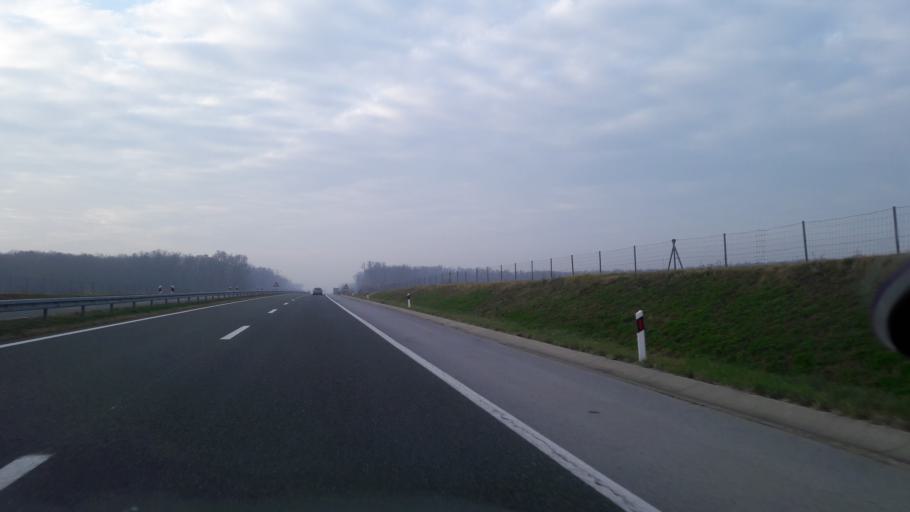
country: HR
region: Osjecko-Baranjska
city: Piskorevci
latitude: 45.2880
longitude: 18.3566
